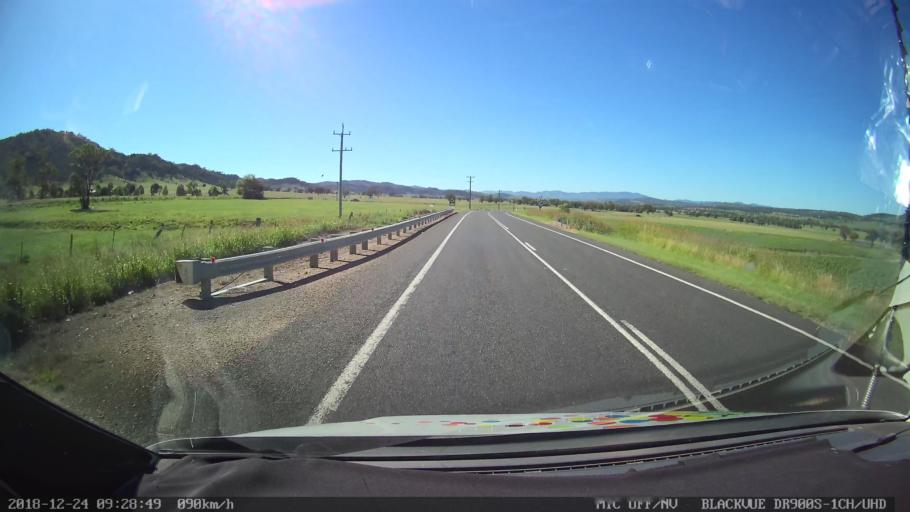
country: AU
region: New South Wales
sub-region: Liverpool Plains
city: Quirindi
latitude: -31.5422
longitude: 150.6917
